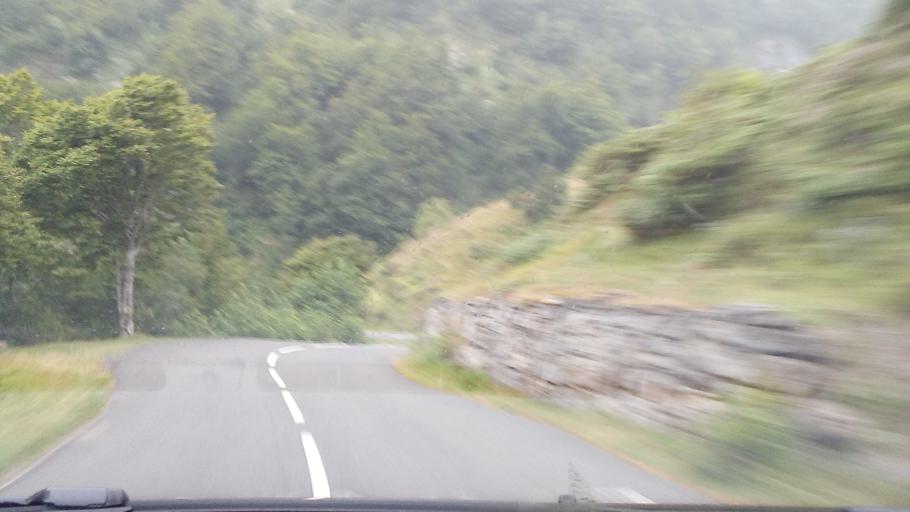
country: FR
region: Aquitaine
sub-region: Departement des Pyrenees-Atlantiques
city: Laruns
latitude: 42.9646
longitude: -0.3028
